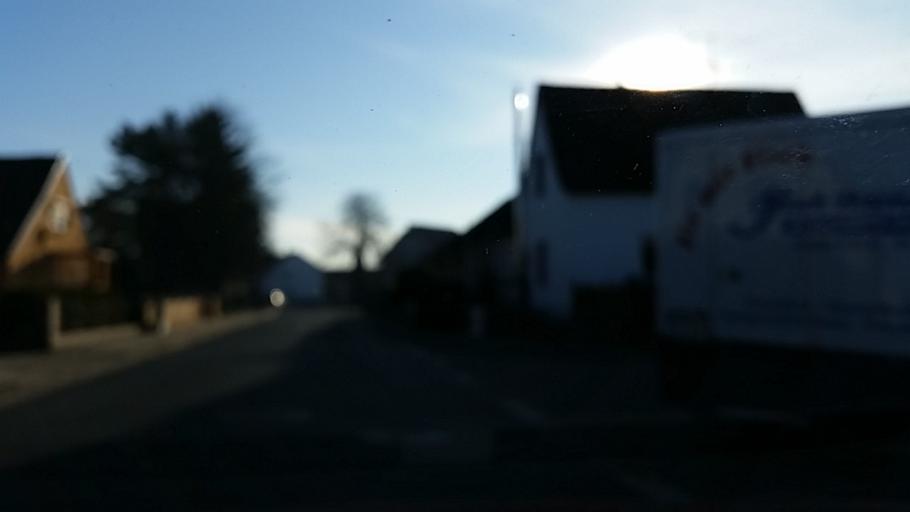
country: DE
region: Lower Saxony
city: Ruhen
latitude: 52.4860
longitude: 10.8404
